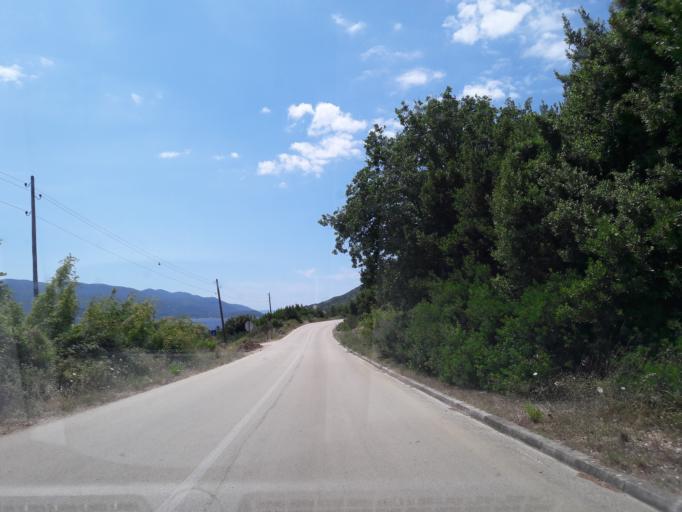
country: HR
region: Dubrovacko-Neretvanska
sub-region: Grad Korcula
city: Zrnovo
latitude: 42.9841
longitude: 17.1041
